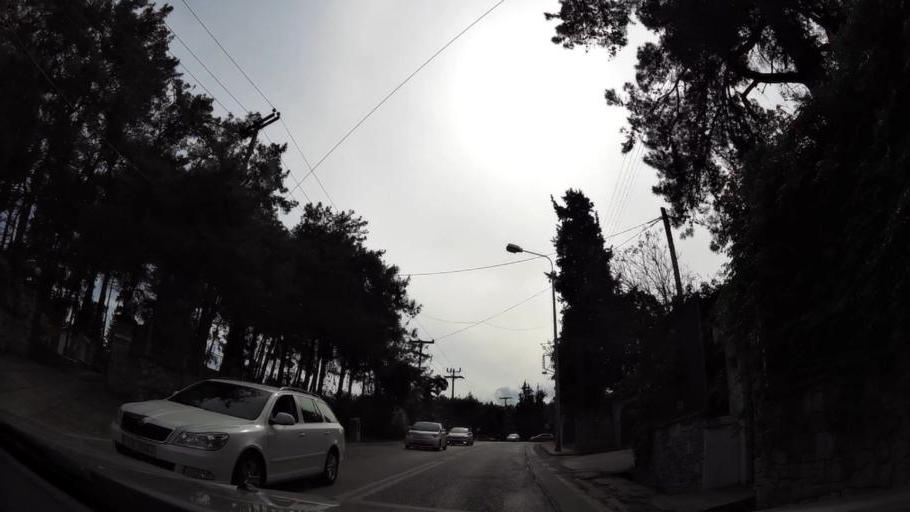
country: GR
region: Central Macedonia
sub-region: Nomos Thessalonikis
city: Panorama
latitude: 40.5937
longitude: 23.0102
